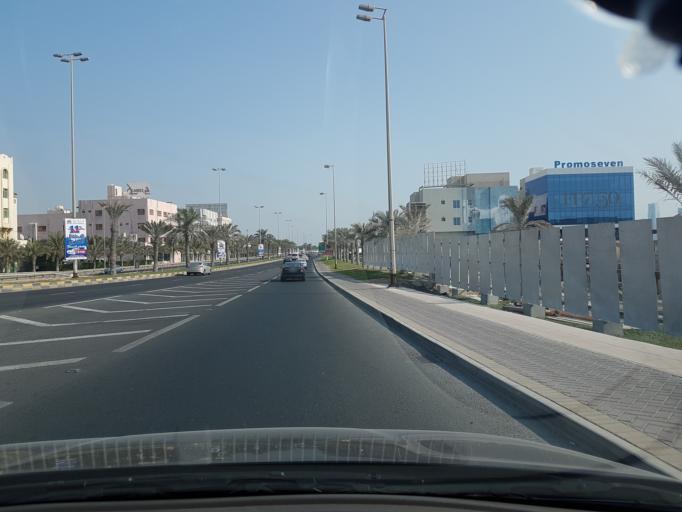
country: BH
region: Muharraq
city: Al Muharraq
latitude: 26.2484
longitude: 50.6069
